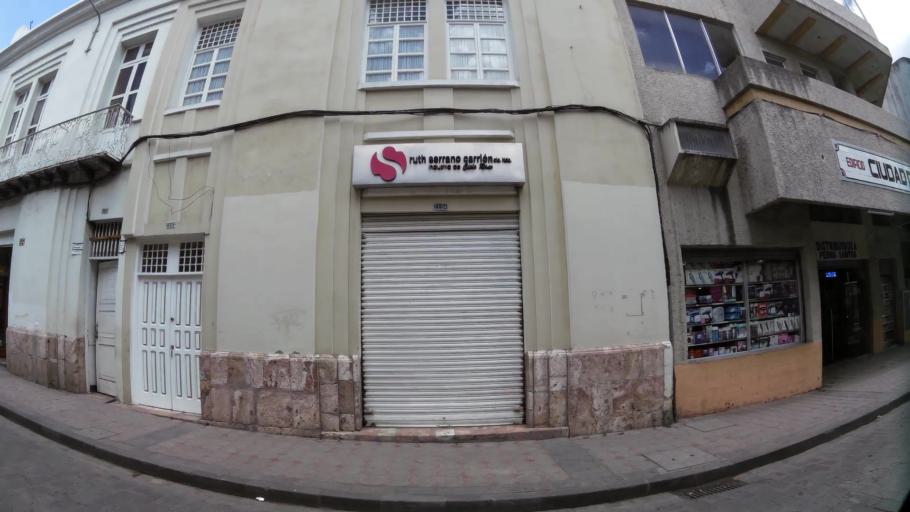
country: EC
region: Azuay
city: Cuenca
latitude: -2.8947
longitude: -79.0025
